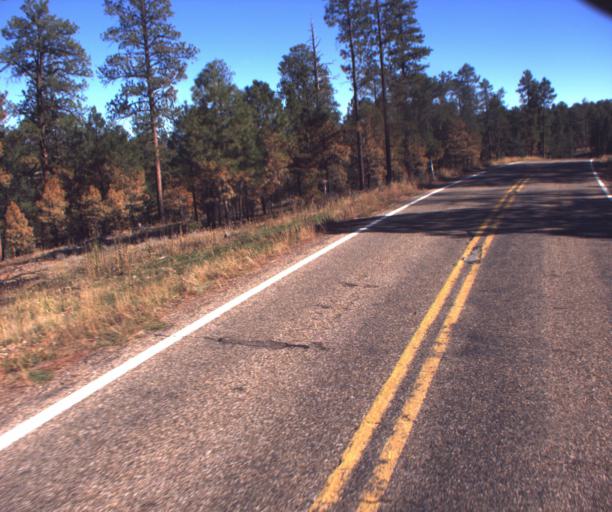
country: US
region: Arizona
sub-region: Coconino County
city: Fredonia
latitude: 36.7337
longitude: -112.1808
